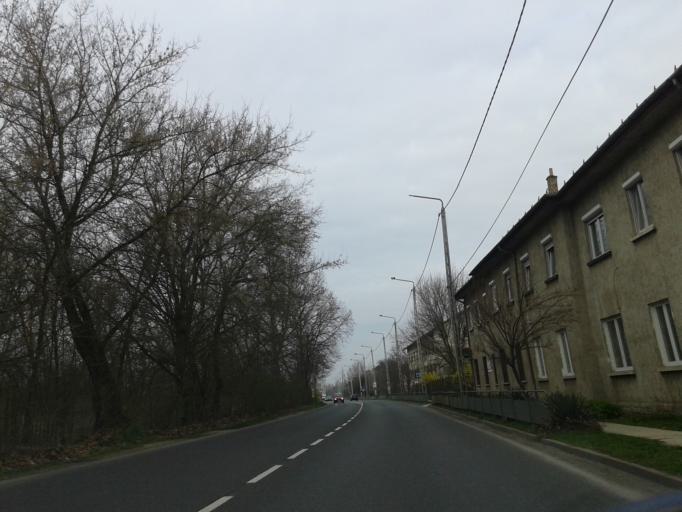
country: HU
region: Komarom-Esztergom
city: Almasfuzito
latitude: 47.7248
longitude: 18.2651
